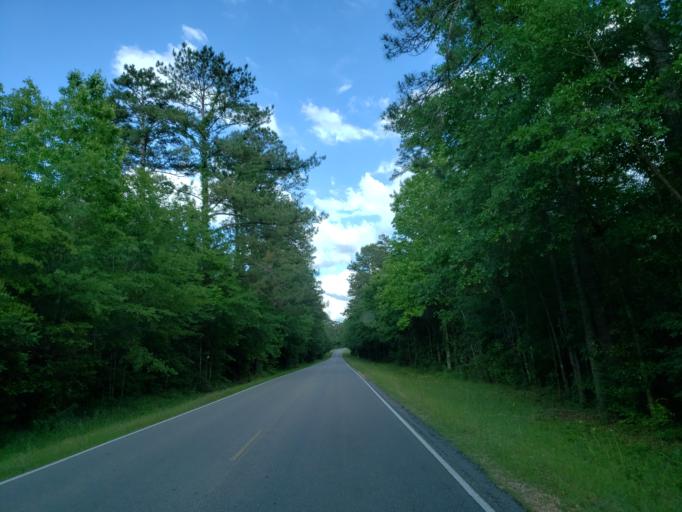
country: US
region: Mississippi
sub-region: Forrest County
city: Petal
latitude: 31.3112
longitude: -89.2267
